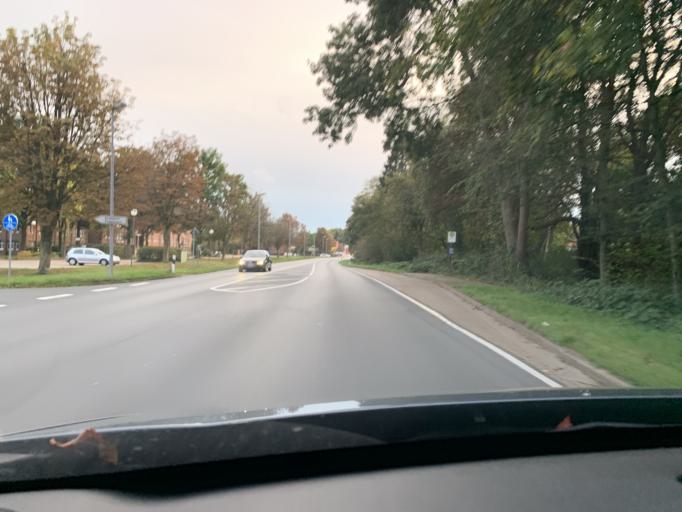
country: DE
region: Lower Saxony
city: Westerstede
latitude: 53.2550
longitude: 7.9336
